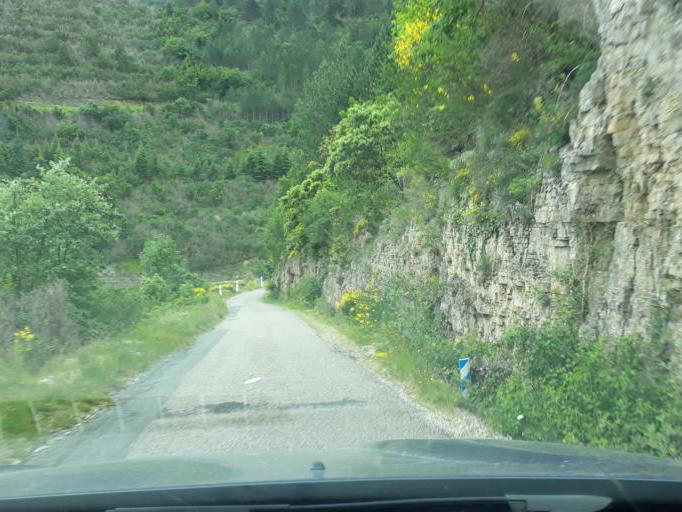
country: FR
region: Languedoc-Roussillon
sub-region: Departement de l'Herault
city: Lodeve
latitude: 43.7922
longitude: 3.2728
